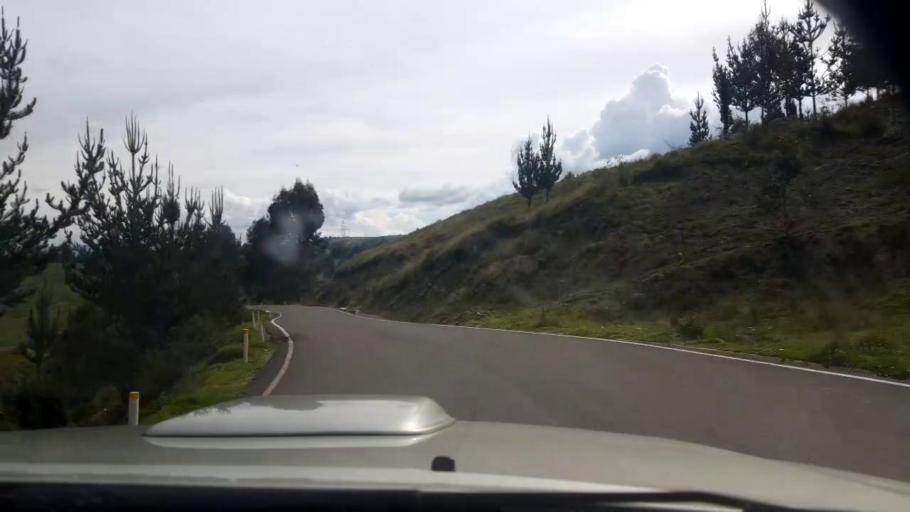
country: PE
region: Ayacucho
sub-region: Provincia de Cangallo
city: Pampa Cangallo
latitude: -13.4488
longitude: -74.1980
